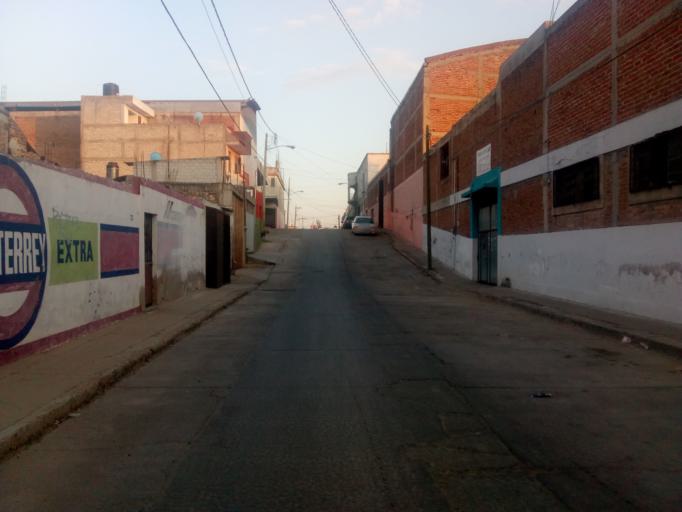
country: MX
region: Guanajuato
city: Leon
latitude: 21.1395
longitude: -101.6836
